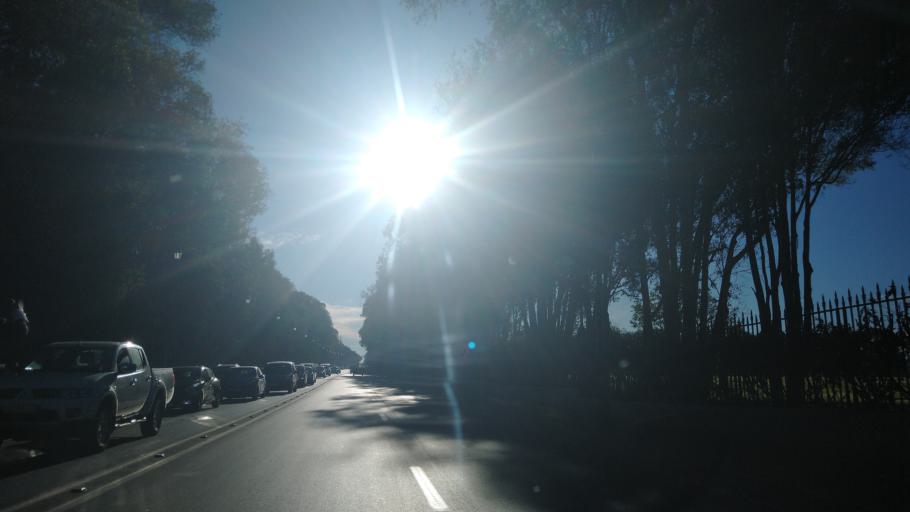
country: MA
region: Rabat-Sale-Zemmour-Zaer
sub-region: Rabat
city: Rabat
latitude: 33.9842
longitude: -6.8483
